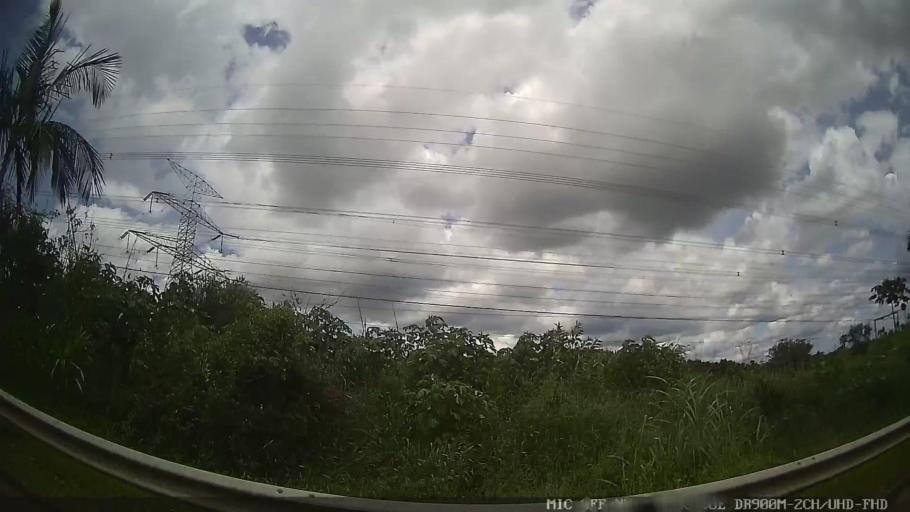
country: BR
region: Sao Paulo
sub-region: Suzano
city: Suzano
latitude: -23.5813
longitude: -46.2551
